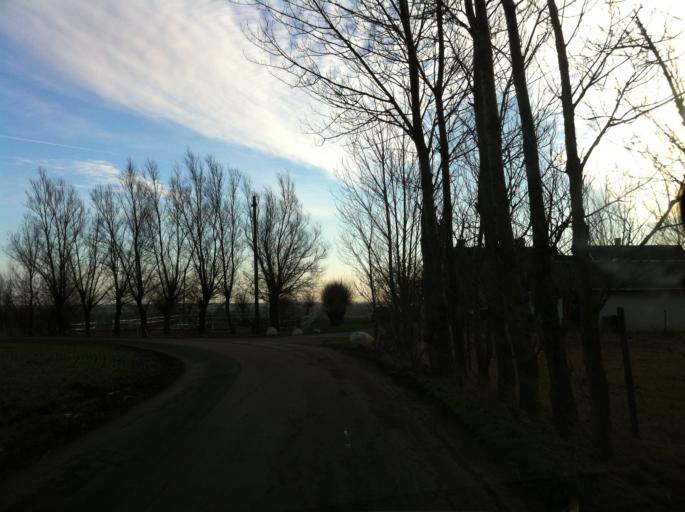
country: SE
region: Skane
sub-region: Landskrona
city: Asmundtorp
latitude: 55.9033
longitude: 12.9233
